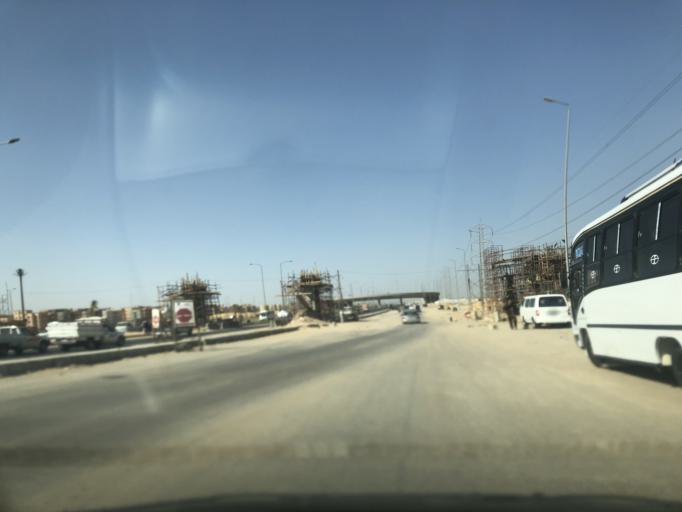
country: EG
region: Al Jizah
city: Madinat Sittah Uktubar
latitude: 29.9296
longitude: 30.9432
